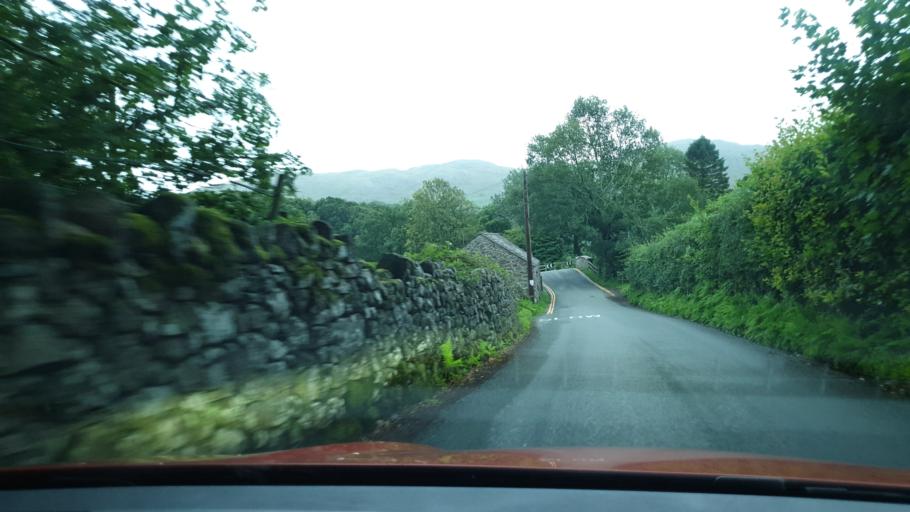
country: GB
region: England
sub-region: Cumbria
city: Seascale
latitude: 54.3878
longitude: -3.3177
